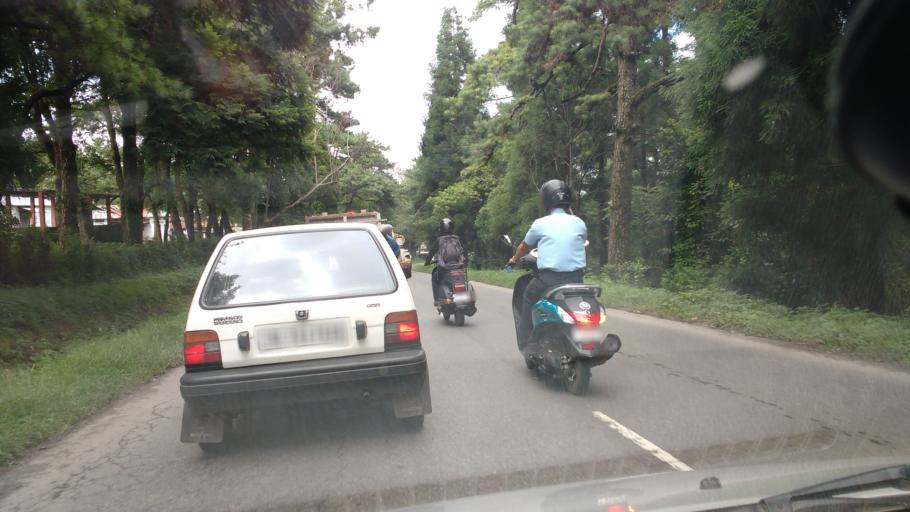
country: IN
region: Meghalaya
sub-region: East Khasi Hills
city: Shillong
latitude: 25.5525
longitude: 91.8441
